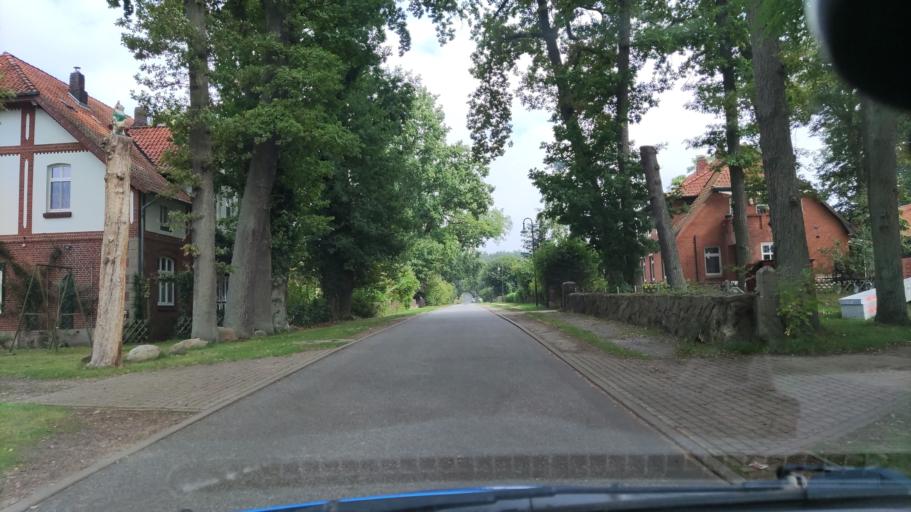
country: DE
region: Lower Saxony
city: Bienenbuttel
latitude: 53.1352
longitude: 10.5123
